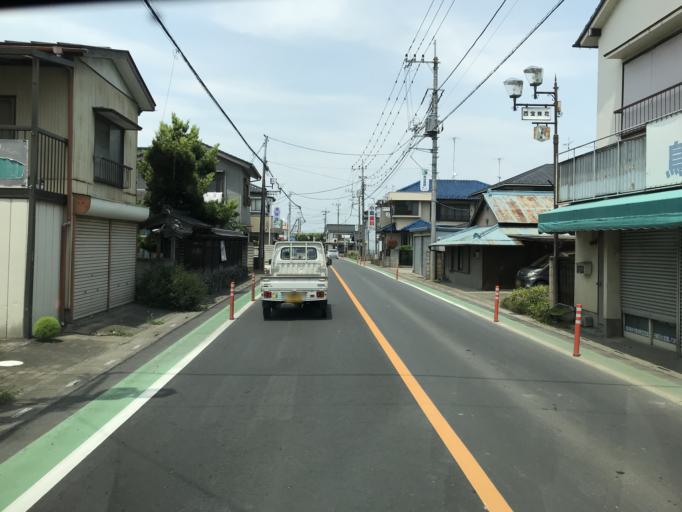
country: JP
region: Ibaraki
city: Sakai
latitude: 36.0315
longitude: 139.8133
